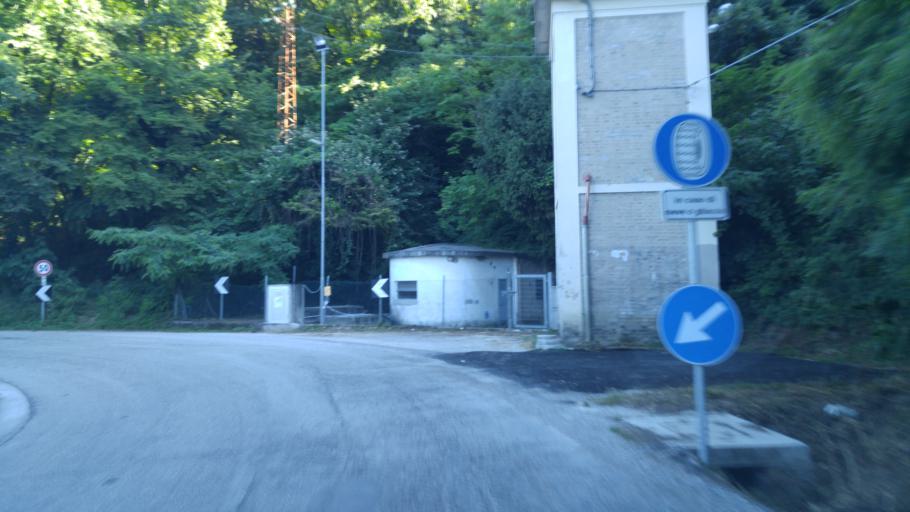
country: IT
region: The Marches
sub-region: Provincia di Pesaro e Urbino
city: Mombaroccio
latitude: 43.7941
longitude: 12.8662
